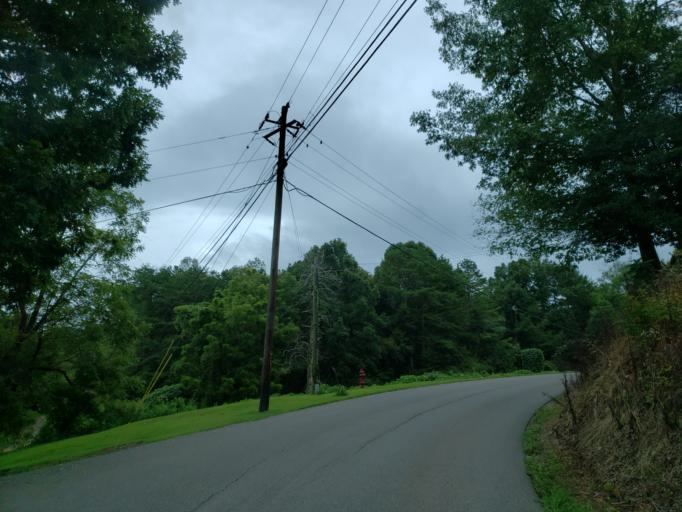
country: US
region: Georgia
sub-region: Gilmer County
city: Ellijay
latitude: 34.6420
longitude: -84.4997
